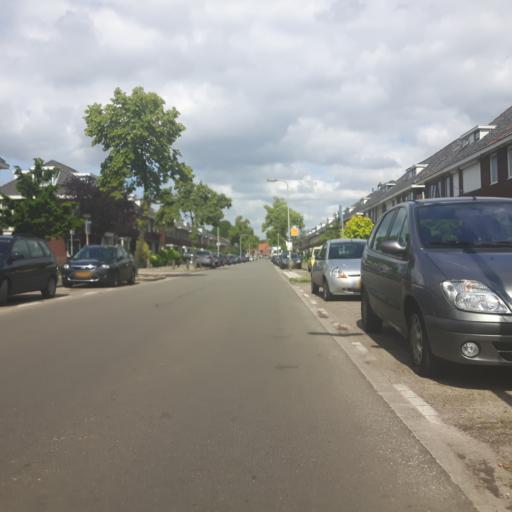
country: NL
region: Overijssel
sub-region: Gemeente Enschede
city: Enschede
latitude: 52.2147
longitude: 6.8681
